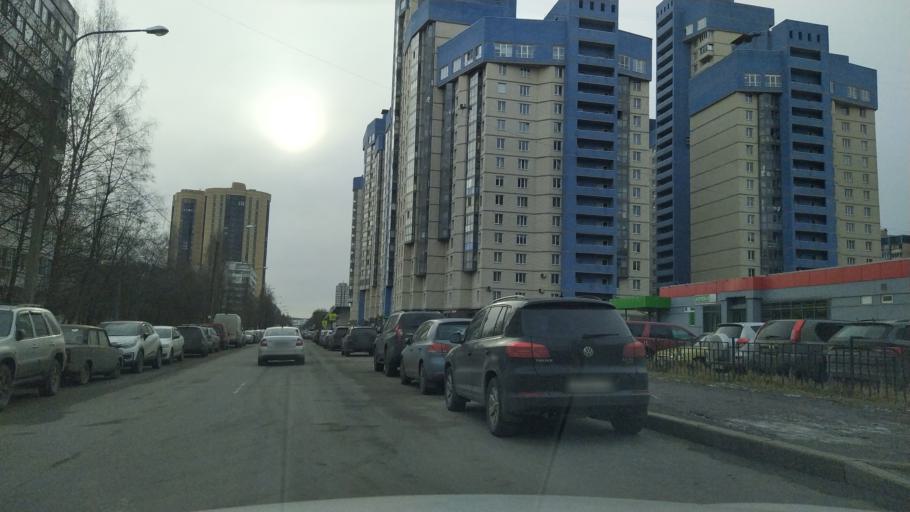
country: RU
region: St.-Petersburg
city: Kolomyagi
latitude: 60.0157
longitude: 30.2804
